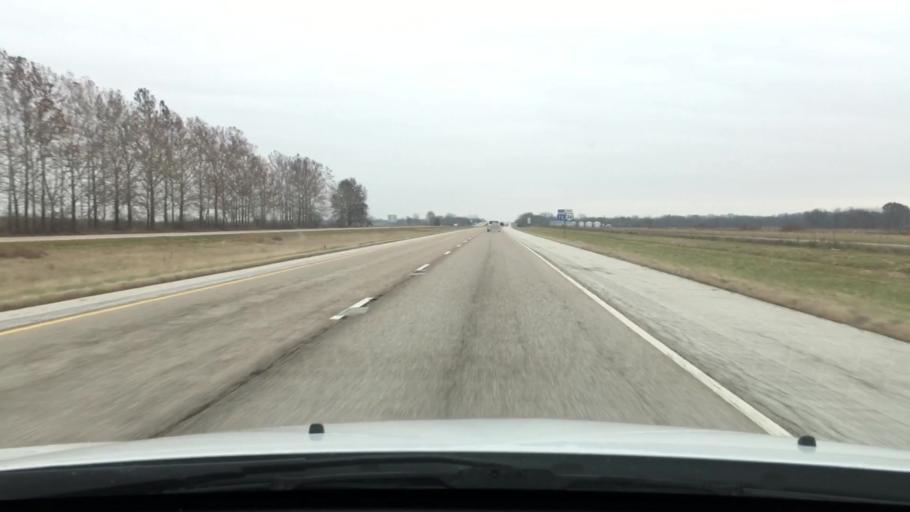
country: US
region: Illinois
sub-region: Scott County
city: Winchester
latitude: 39.6812
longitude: -90.4474
